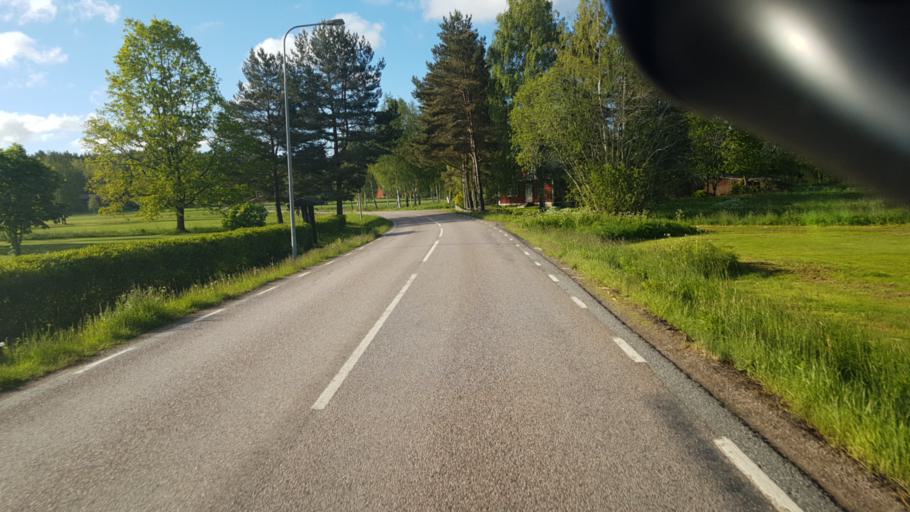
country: SE
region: Vaermland
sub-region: Arvika Kommun
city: Arvika
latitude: 59.5736
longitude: 12.5541
